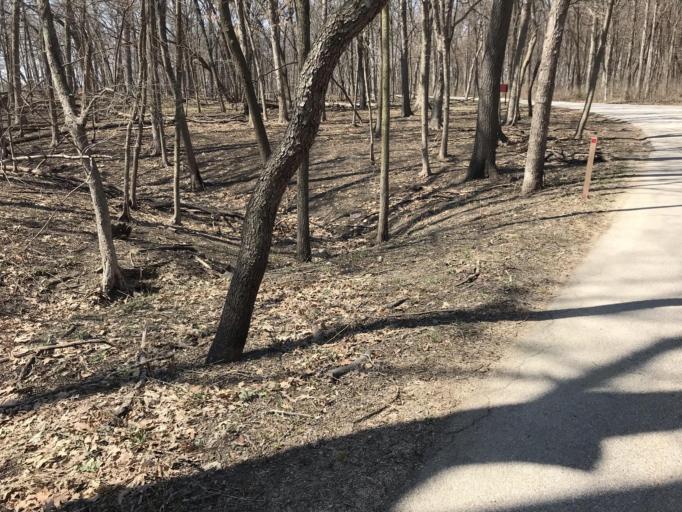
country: US
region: Illinois
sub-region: DuPage County
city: Lisle
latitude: 41.8141
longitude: -88.0454
